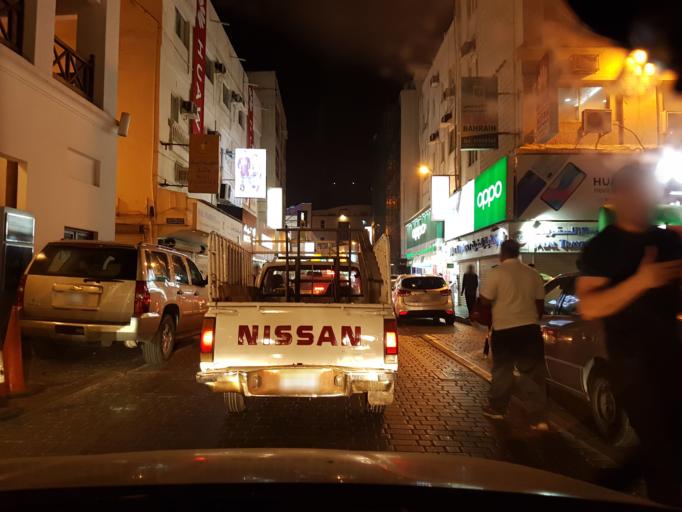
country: BH
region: Manama
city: Manama
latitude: 26.2338
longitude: 50.5756
